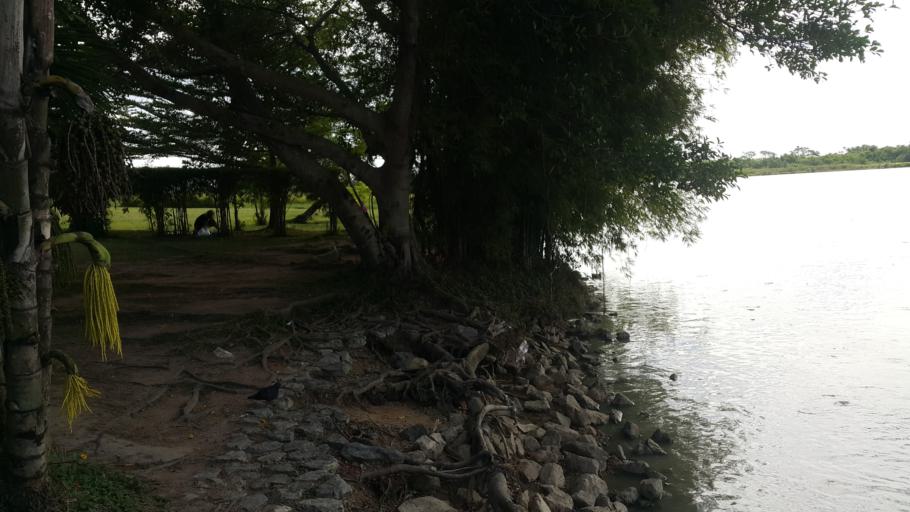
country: TH
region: Rayong
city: Ban Chang
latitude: 12.7890
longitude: 100.9544
